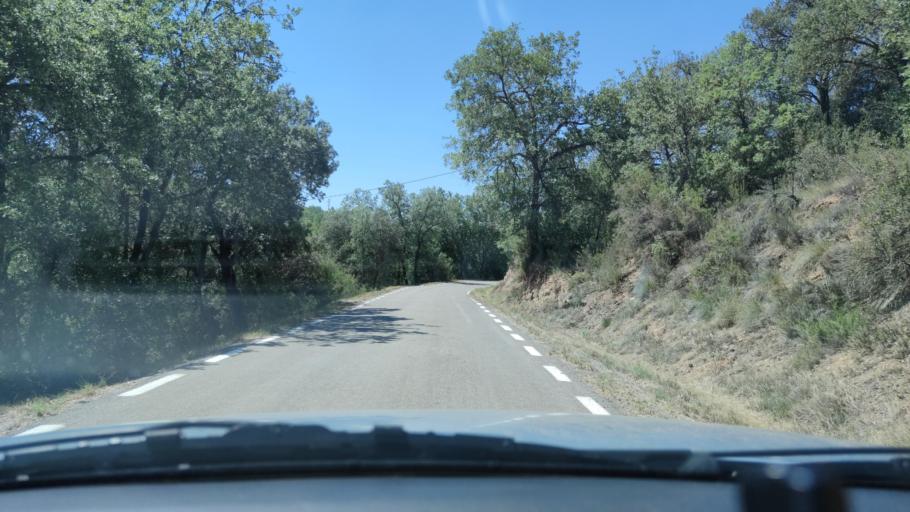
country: ES
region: Catalonia
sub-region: Provincia de Lleida
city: Tora de Riubregos
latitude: 41.8505
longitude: 1.4268
